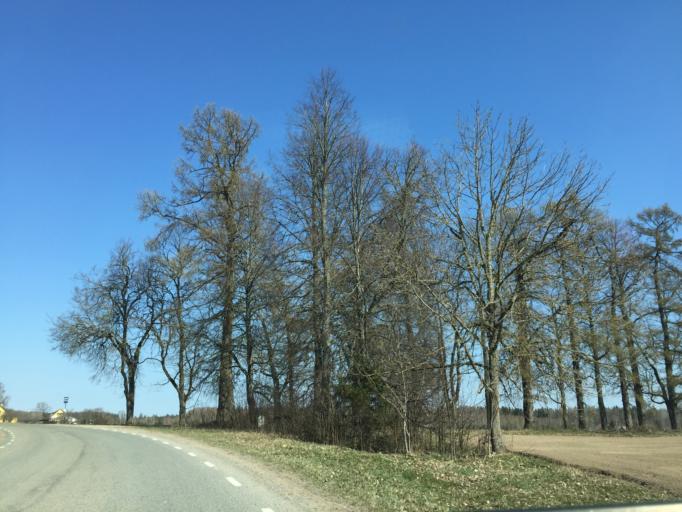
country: EE
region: Tartu
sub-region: Tartu linn
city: Tartu
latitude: 58.5274
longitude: 26.8767
